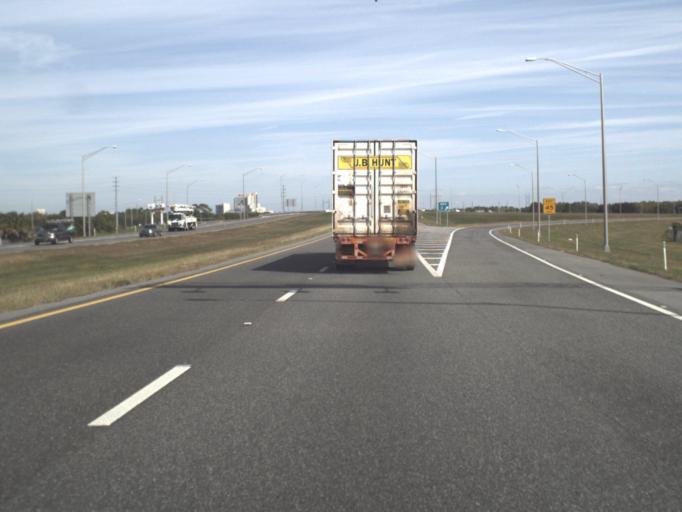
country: US
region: Florida
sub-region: Osceola County
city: Celebration
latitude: 28.3369
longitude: -81.5199
